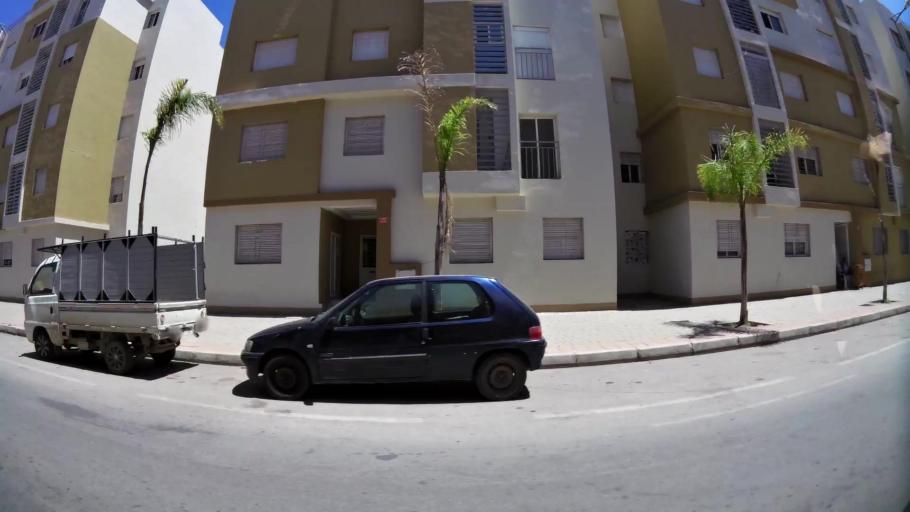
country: MA
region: Oriental
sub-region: Oujda-Angad
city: Oujda
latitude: 34.6621
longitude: -1.9196
